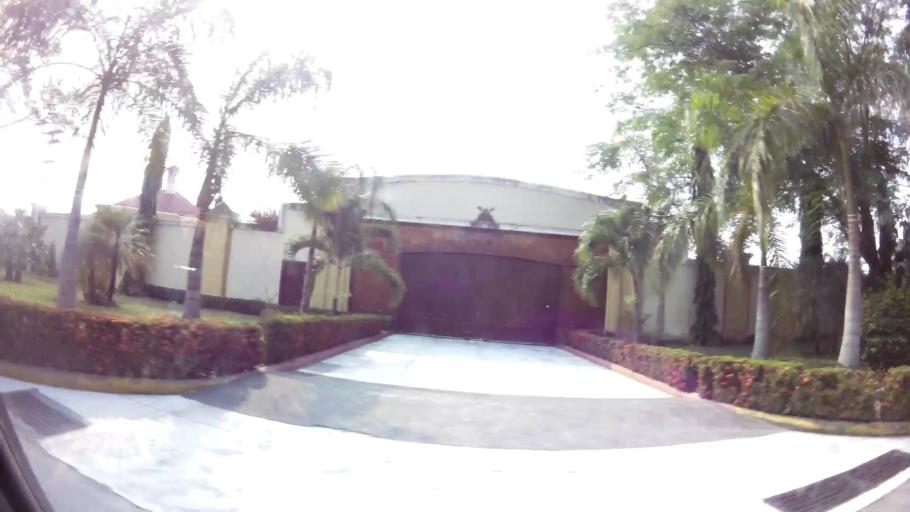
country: HN
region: Cortes
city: El Zapotal del Norte
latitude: 15.5209
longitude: -88.0419
